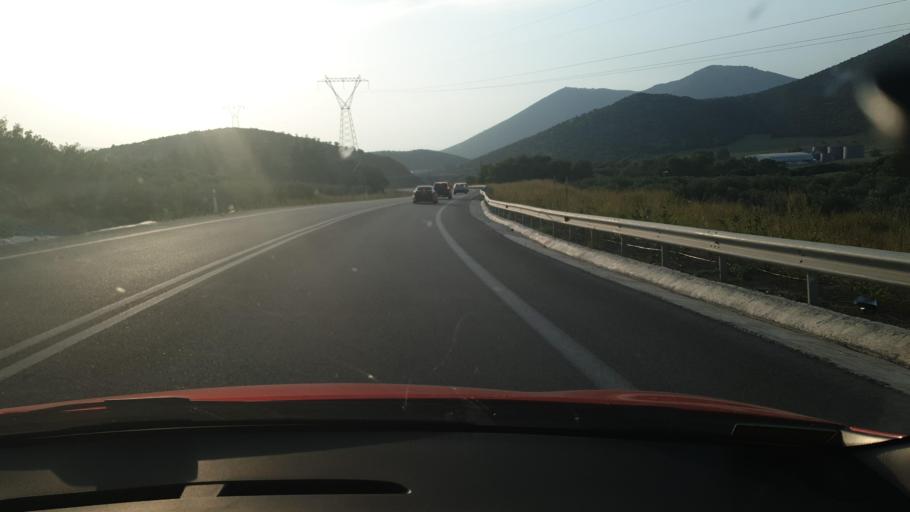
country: GR
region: Central Macedonia
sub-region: Nomos Chalkidikis
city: Galatista
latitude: 40.4641
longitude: 23.2160
